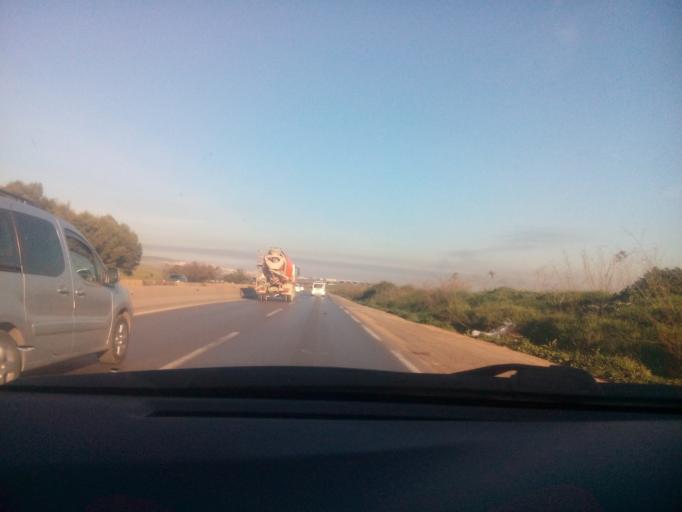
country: DZ
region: Oran
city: Bir el Djir
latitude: 35.7578
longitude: -0.4754
